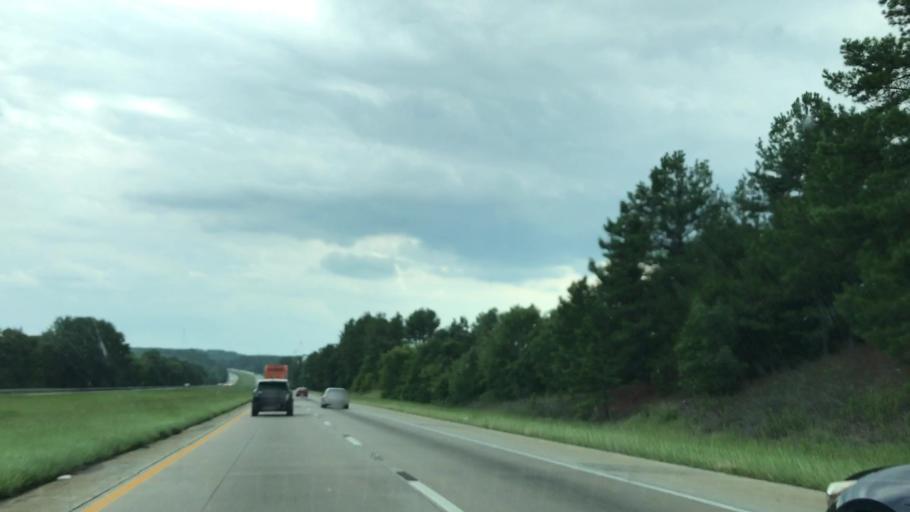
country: US
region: South Carolina
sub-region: Fairfield County
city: Winnsboro Mills
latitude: 34.3375
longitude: -81.0036
